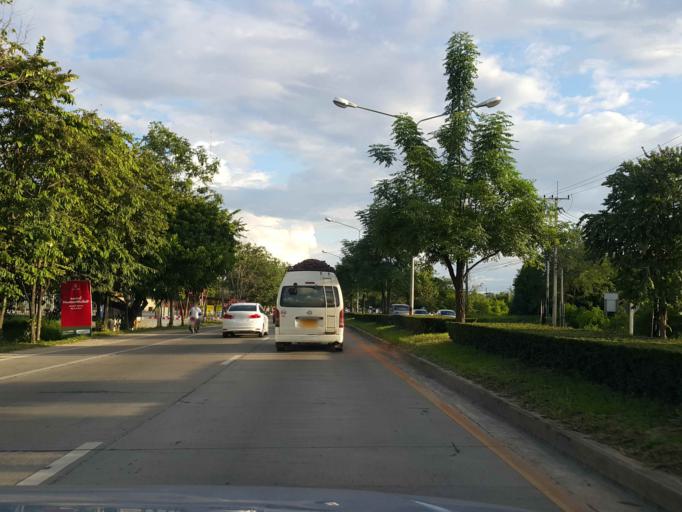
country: TH
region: Chiang Mai
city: San Sai
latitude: 18.8451
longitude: 99.0136
